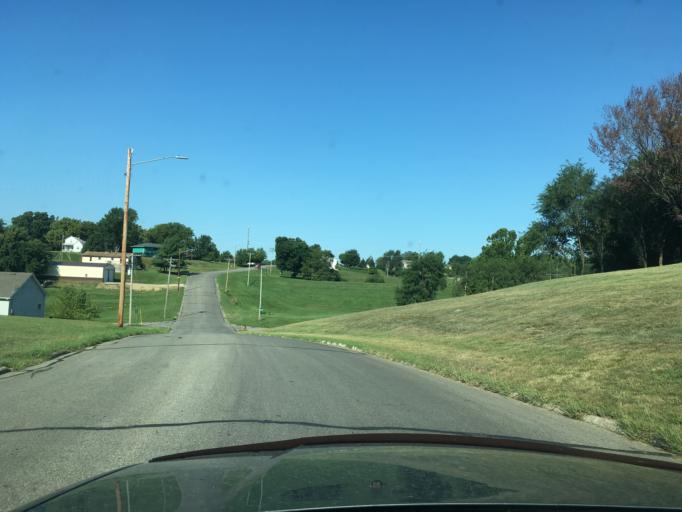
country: US
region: Kansas
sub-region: Atchison County
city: Atchison
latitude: 39.5787
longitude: -95.1205
